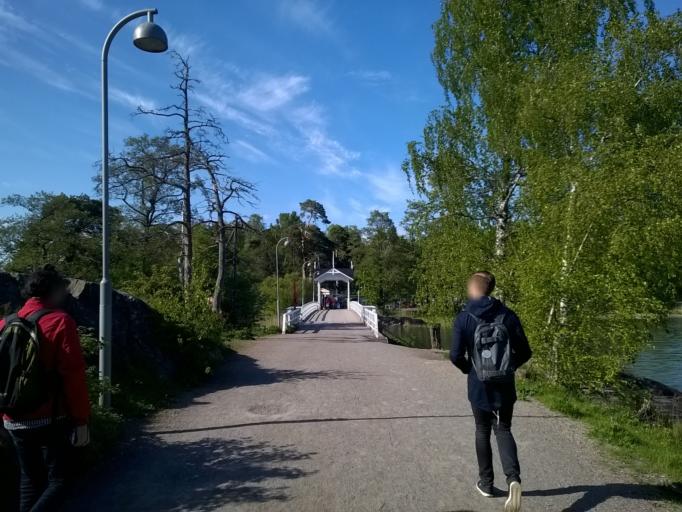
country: FI
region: Uusimaa
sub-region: Helsinki
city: Teekkarikylae
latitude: 60.1875
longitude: 24.8846
